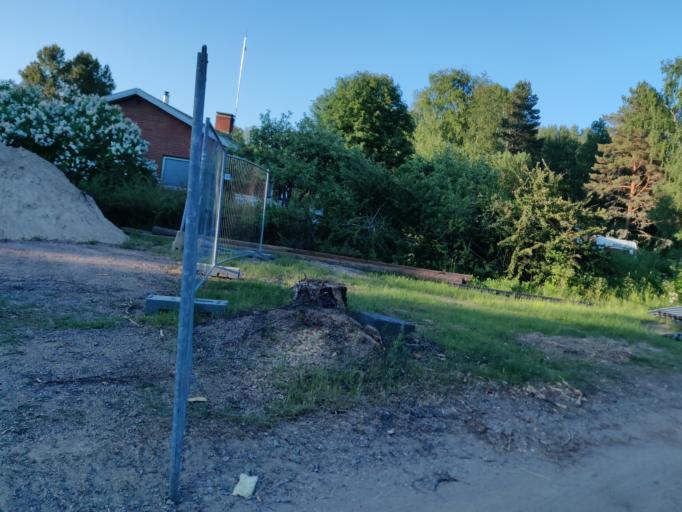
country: SE
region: Vaermland
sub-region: Hagfors Kommun
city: Hagfors
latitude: 60.0034
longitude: 13.5920
